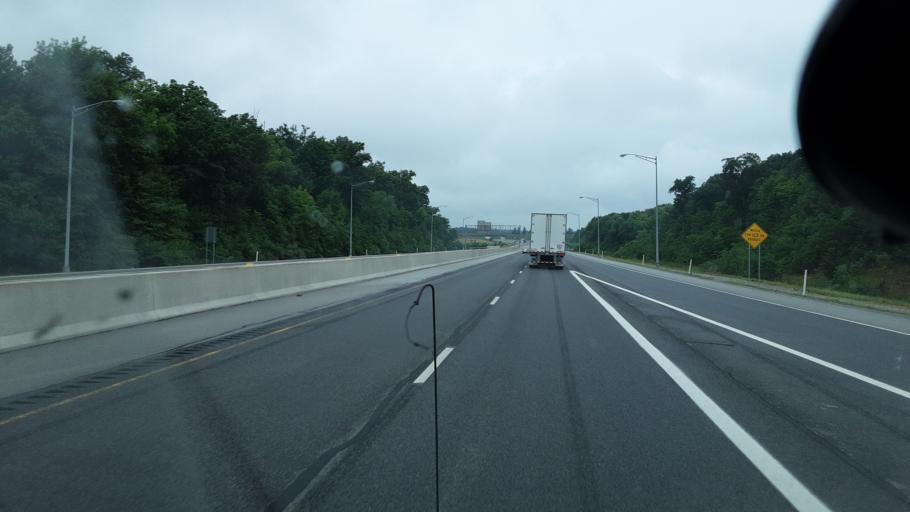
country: US
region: Indiana
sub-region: Allen County
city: New Haven
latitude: 40.9824
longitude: -85.0903
